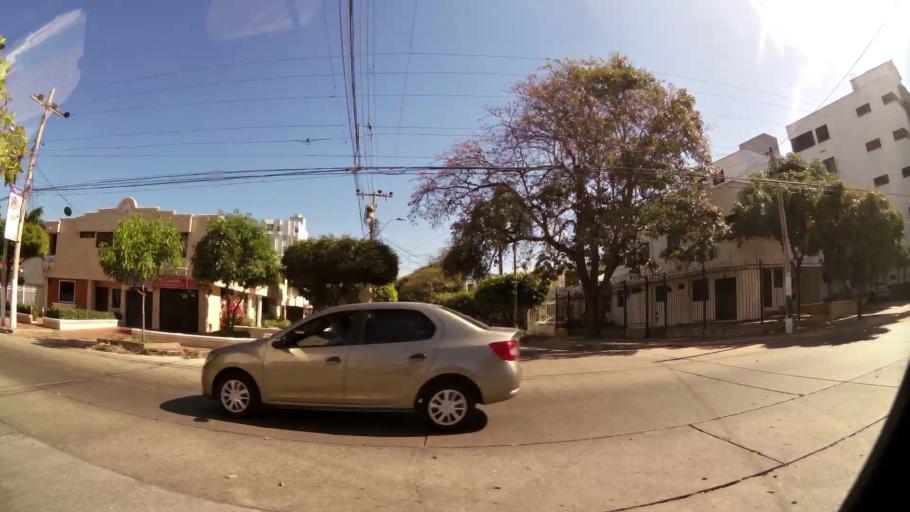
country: CO
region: Atlantico
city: Barranquilla
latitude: 11.0008
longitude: -74.7929
